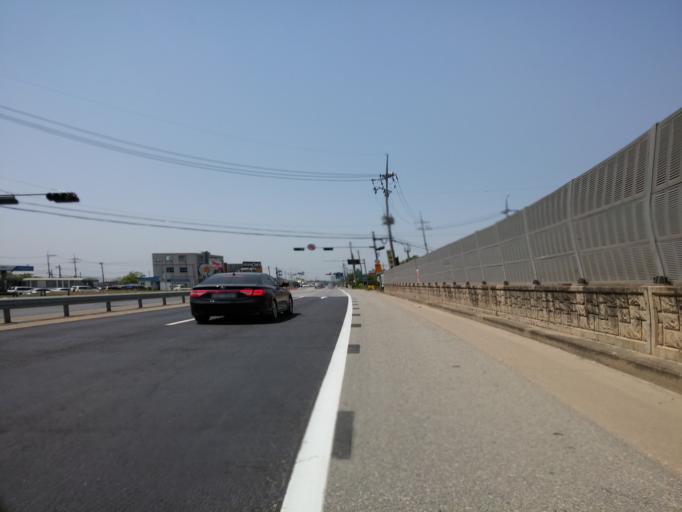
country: KR
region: Chungcheongnam-do
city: Nonsan
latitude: 36.2142
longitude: 127.1297
